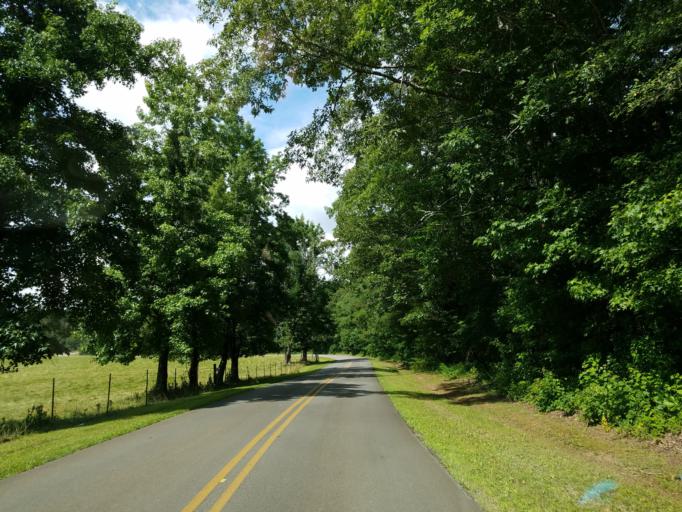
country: US
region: Georgia
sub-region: Pickens County
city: Nelson
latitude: 34.3962
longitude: -84.3753
